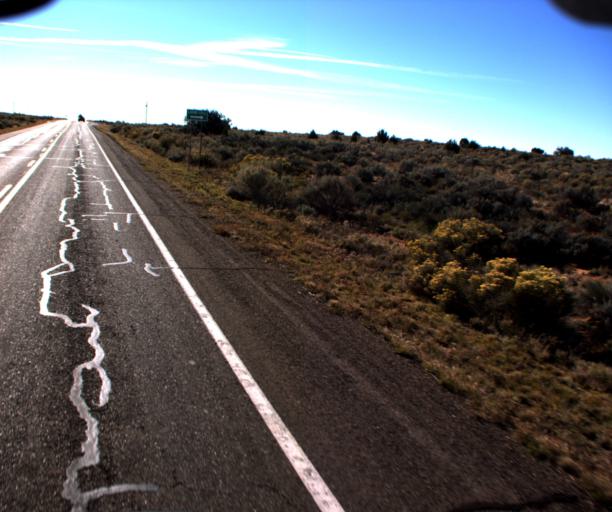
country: US
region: Arizona
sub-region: Mohave County
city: Colorado City
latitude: 36.9061
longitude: -112.9238
